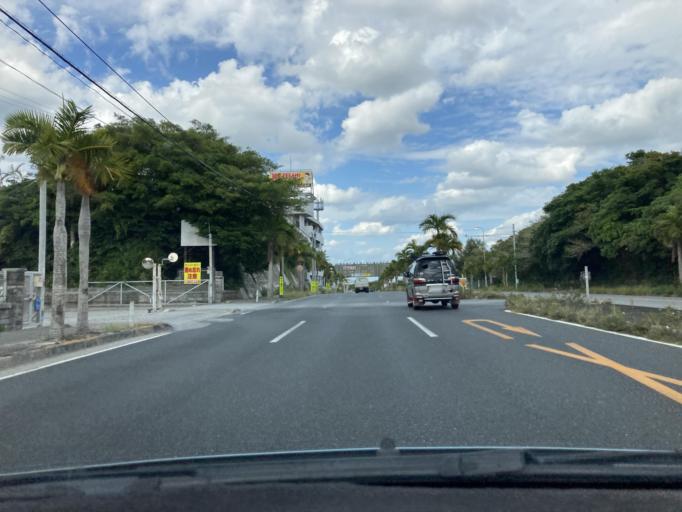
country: JP
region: Okinawa
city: Chatan
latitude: 26.3347
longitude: 127.7515
